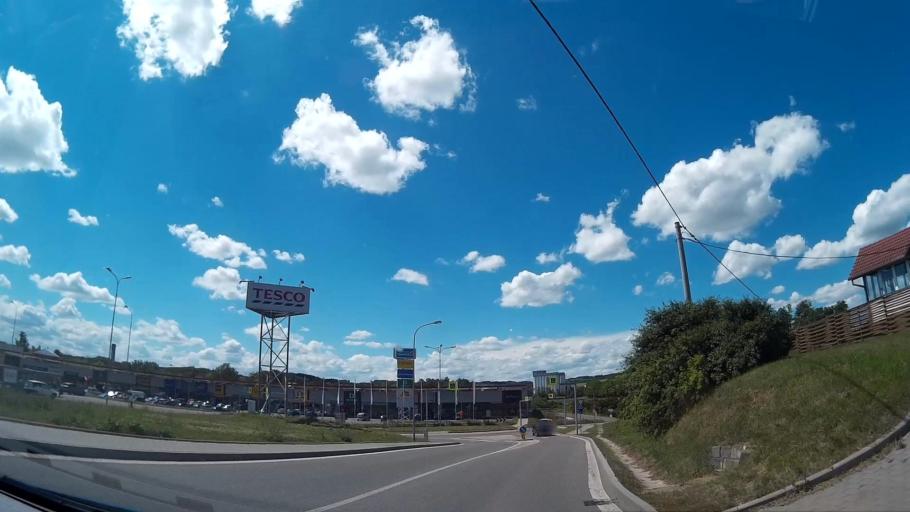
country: CZ
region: South Moravian
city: Ivancice
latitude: 49.1041
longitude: 16.3655
